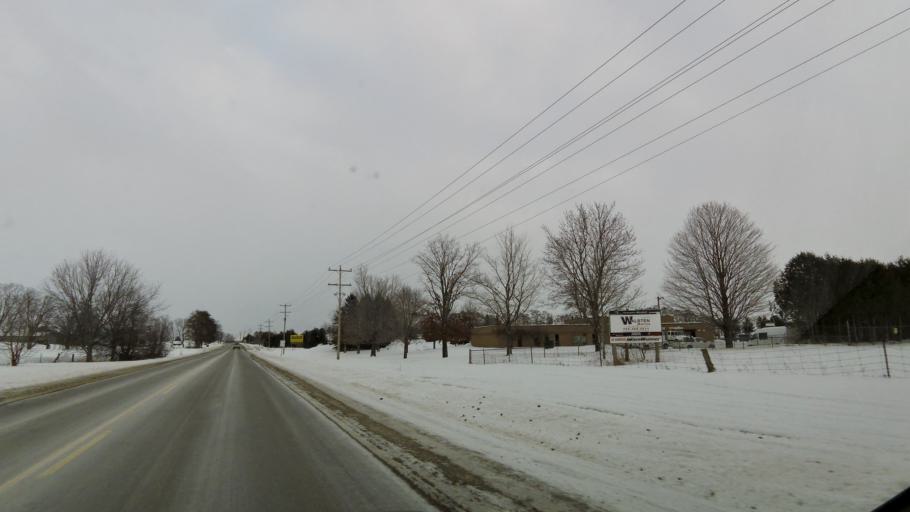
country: CA
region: Ontario
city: Omemee
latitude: 44.5192
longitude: -78.7968
